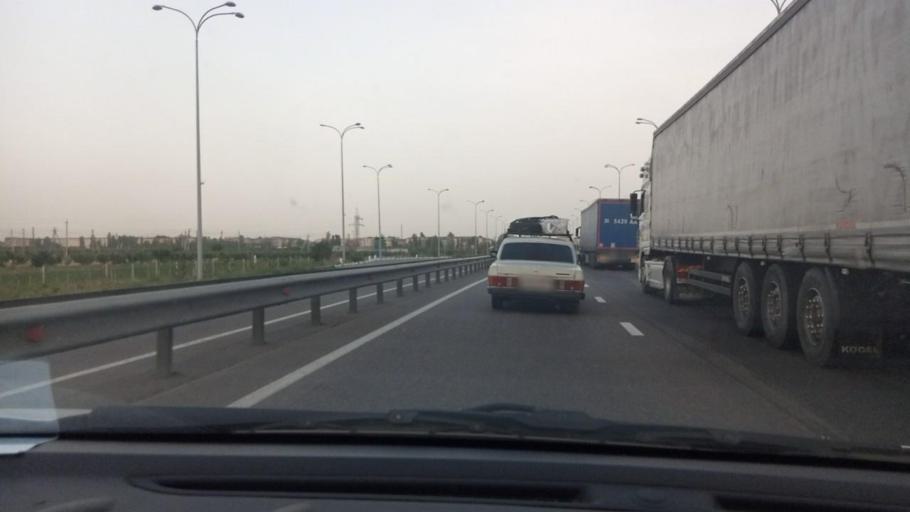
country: UZ
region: Toshkent
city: Ohangaron
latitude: 40.9132
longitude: 69.6126
